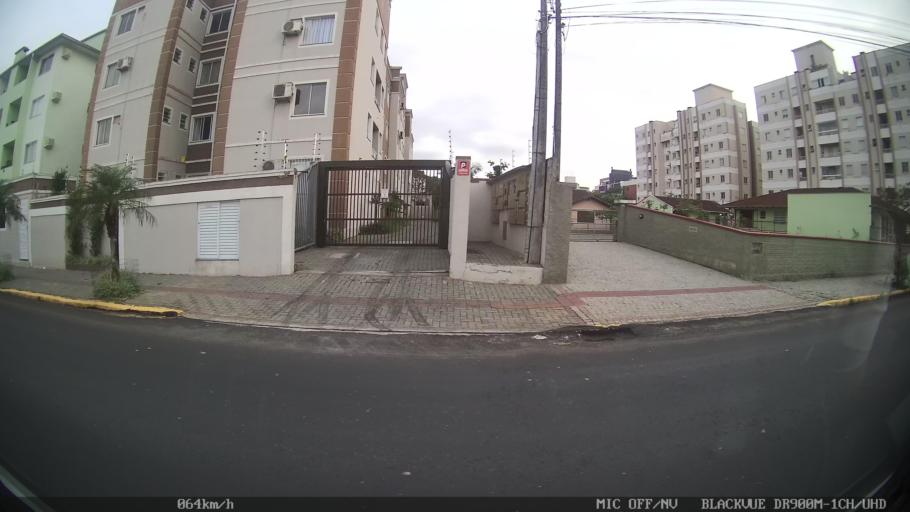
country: BR
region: Santa Catarina
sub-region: Joinville
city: Joinville
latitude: -26.2900
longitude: -48.8679
